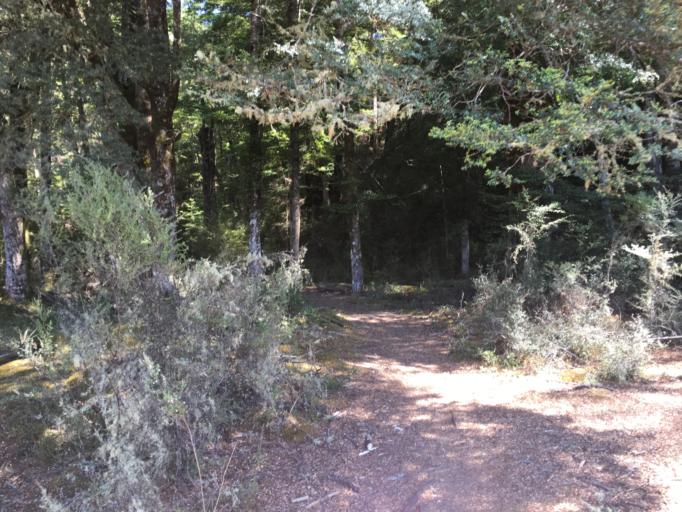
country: NZ
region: Southland
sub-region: Southland District
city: Te Anau
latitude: -45.4862
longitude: 167.6851
